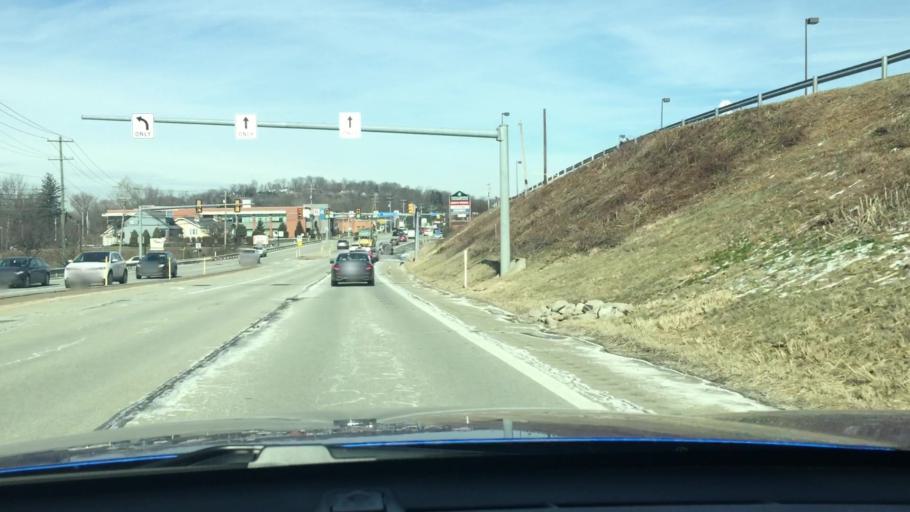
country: US
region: Pennsylvania
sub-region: Washington County
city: Thompsonville
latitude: 40.2687
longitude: -80.1286
